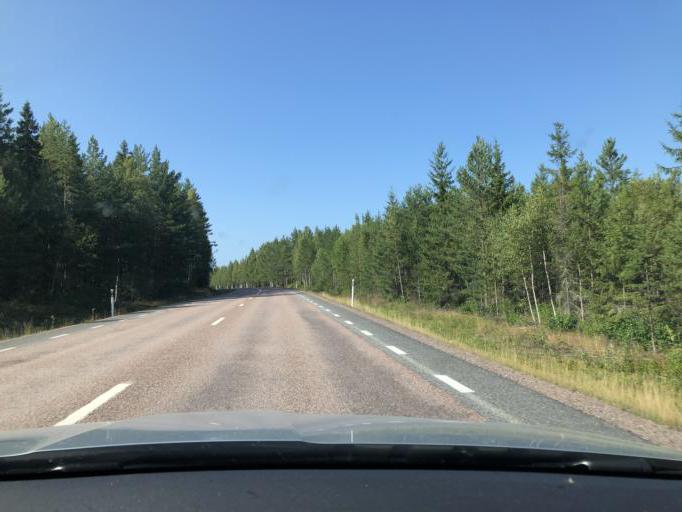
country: SE
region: Dalarna
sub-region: Saters Kommun
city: Saeter
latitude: 60.4943
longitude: 15.7595
